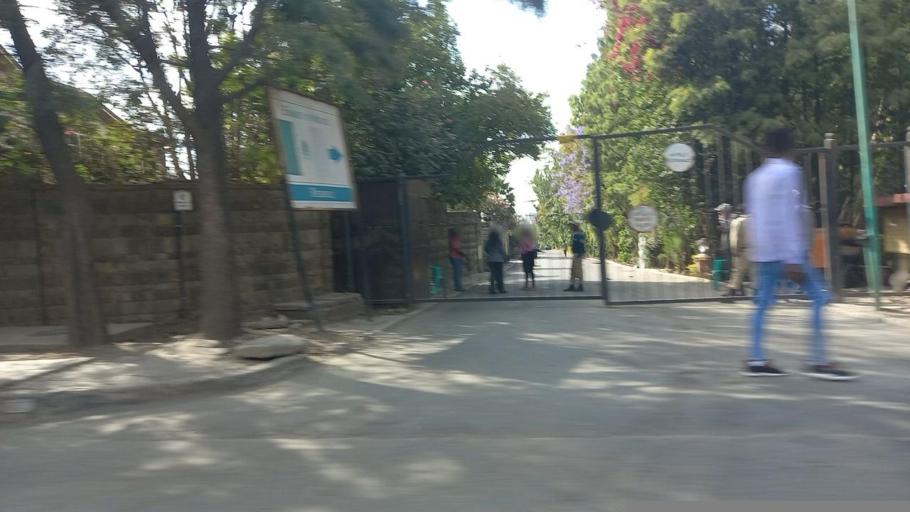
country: ET
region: Adis Abeba
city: Addis Ababa
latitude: 9.0061
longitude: 38.8195
